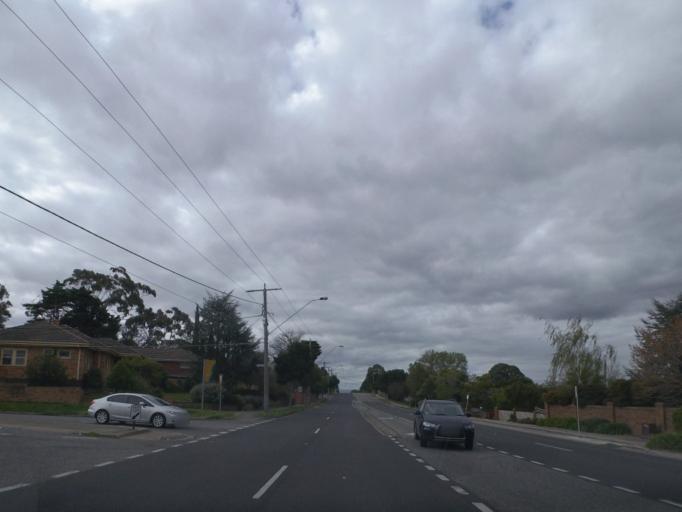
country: AU
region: Victoria
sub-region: Manningham
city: Templestowe Lower
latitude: -37.7730
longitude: 145.1148
